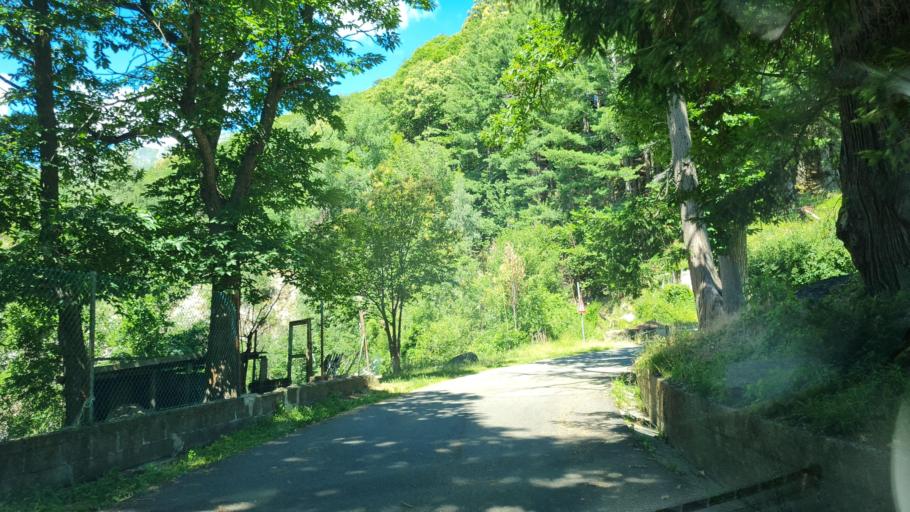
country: IT
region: Piedmont
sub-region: Provincia di Torino
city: Quincinetto
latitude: 45.5548
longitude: 7.7939
